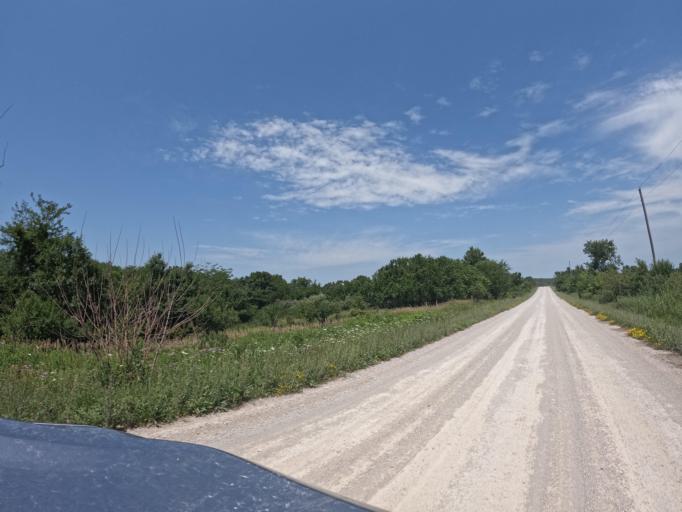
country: US
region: Iowa
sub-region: Appanoose County
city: Centerville
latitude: 40.7951
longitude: -92.9160
